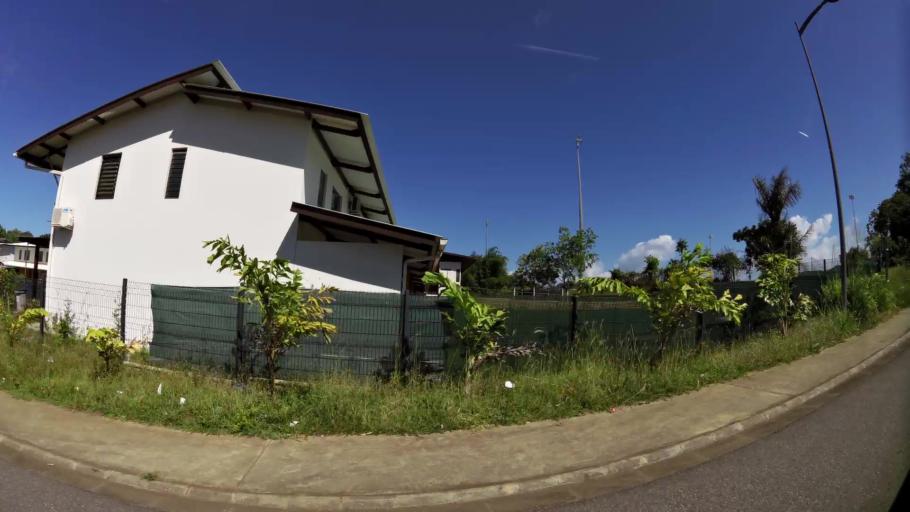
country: GF
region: Guyane
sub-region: Guyane
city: Remire-Montjoly
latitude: 4.9142
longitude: -52.2770
